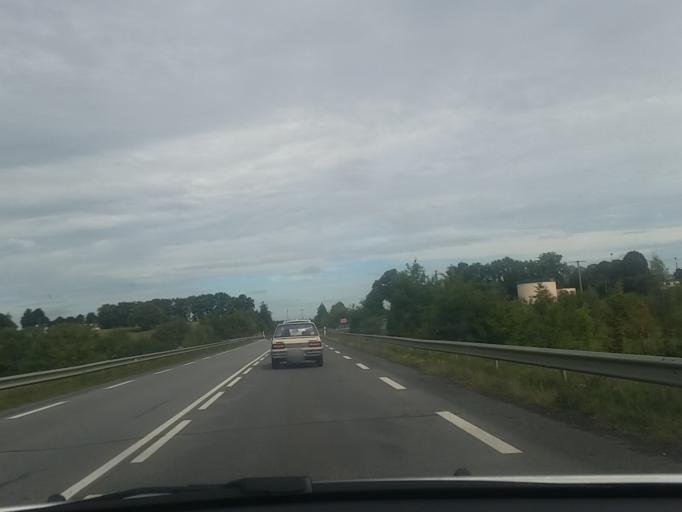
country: FR
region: Brittany
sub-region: Departement d'Ille-et-Vilaine
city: Martigne-Ferchaud
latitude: 47.8251
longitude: -1.3276
